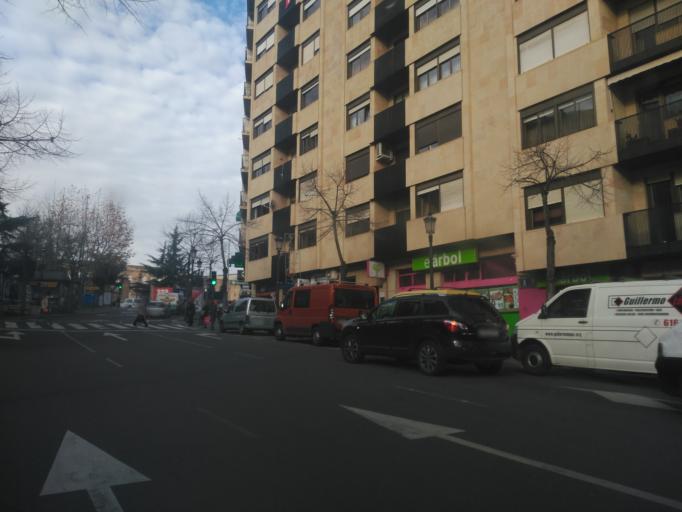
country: ES
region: Castille and Leon
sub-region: Provincia de Salamanca
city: Salamanca
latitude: 40.9675
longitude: -5.6670
